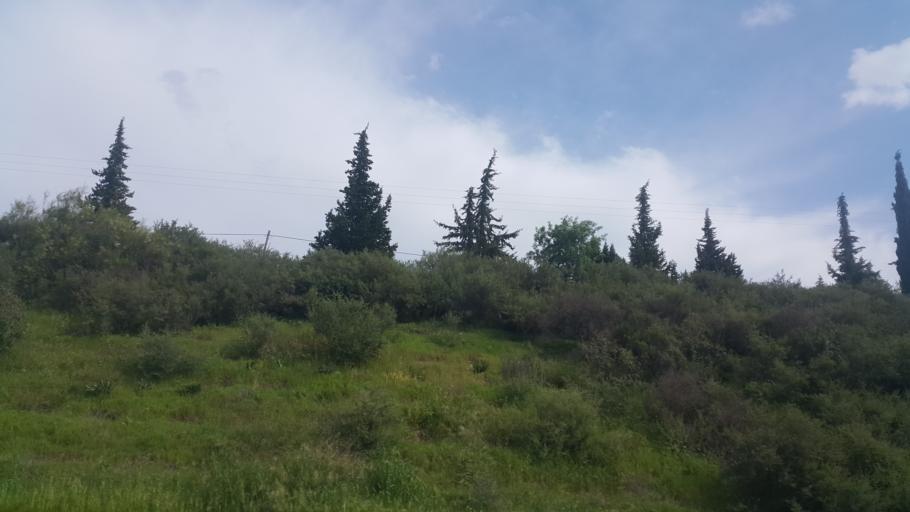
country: TR
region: Mersin
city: Kazanli
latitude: 36.9364
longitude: 34.7168
